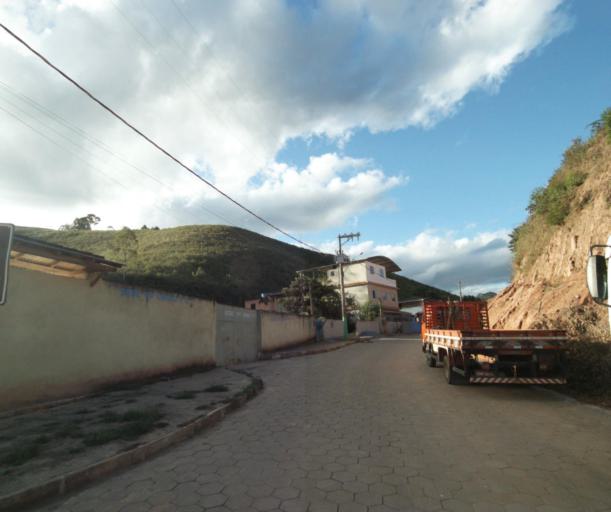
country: BR
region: Espirito Santo
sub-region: Guacui
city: Guacui
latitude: -20.6254
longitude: -41.6881
